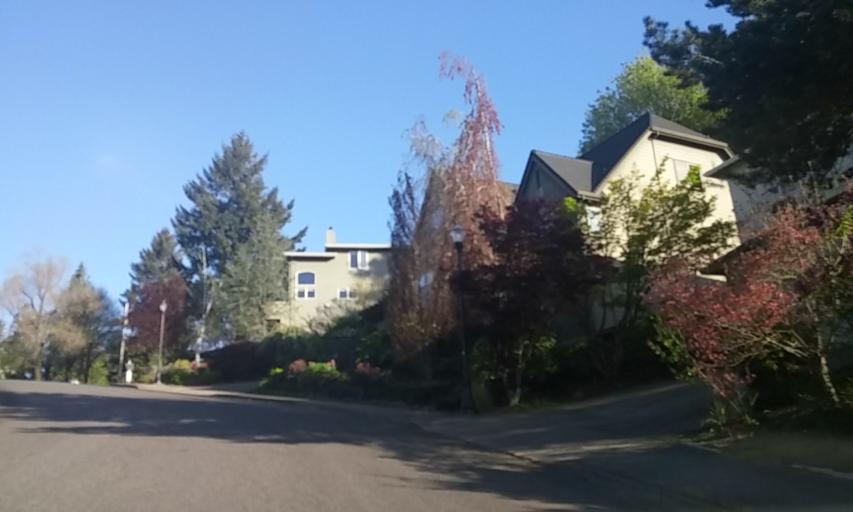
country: US
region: Oregon
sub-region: Washington County
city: West Haven
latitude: 45.5432
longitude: -122.7826
